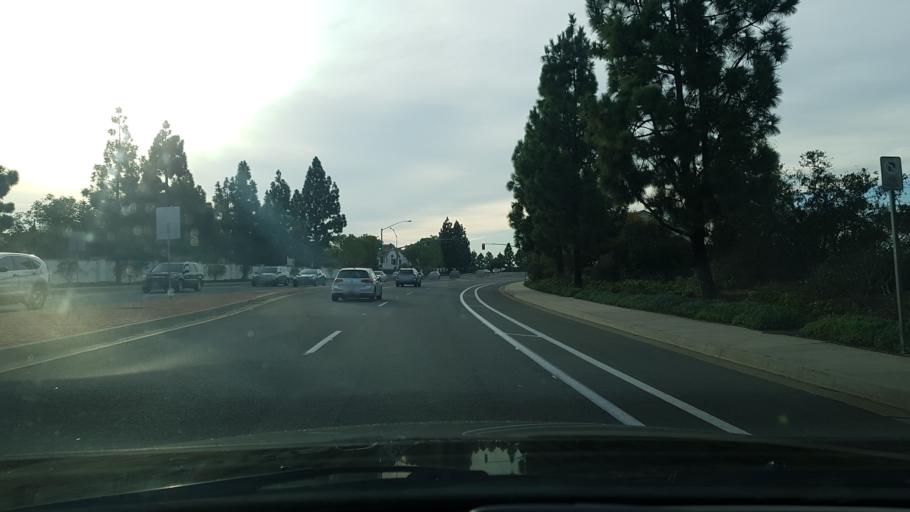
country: US
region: California
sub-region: San Diego County
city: Fairbanks Ranch
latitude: 32.9185
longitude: -117.1837
